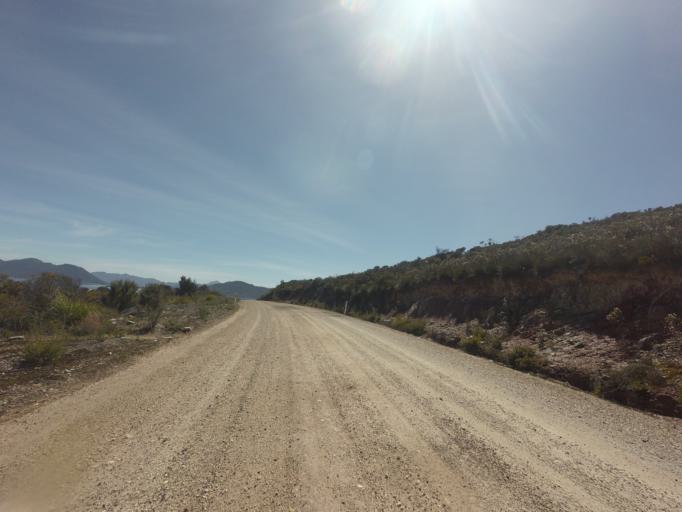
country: AU
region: Tasmania
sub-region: Huon Valley
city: Geeveston
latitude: -43.0309
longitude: 146.3412
